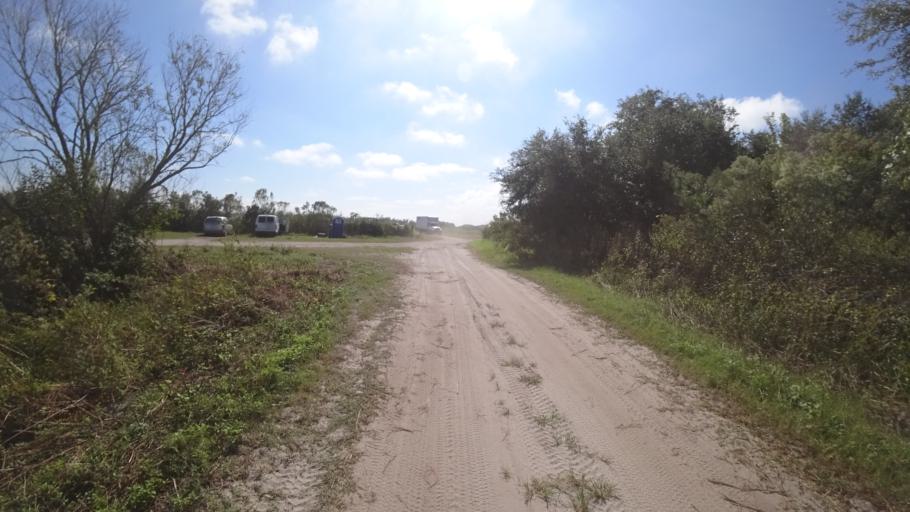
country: US
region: Florida
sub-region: DeSoto County
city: Arcadia
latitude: 27.2925
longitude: -82.0741
